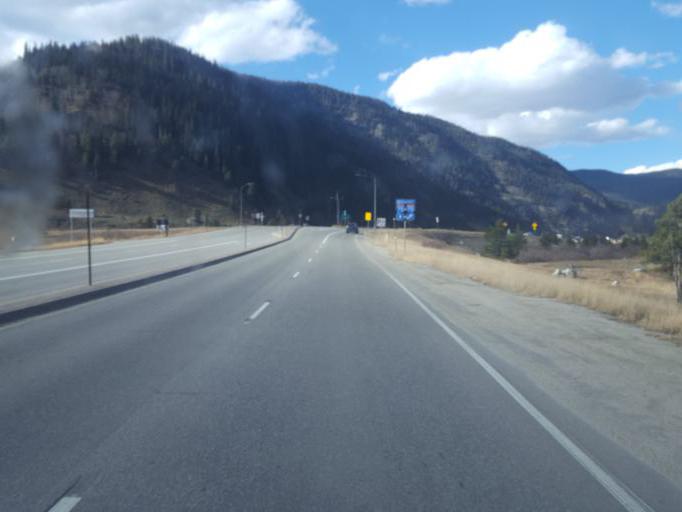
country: US
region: Colorado
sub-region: Summit County
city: Frisco
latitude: 39.5046
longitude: -106.1417
